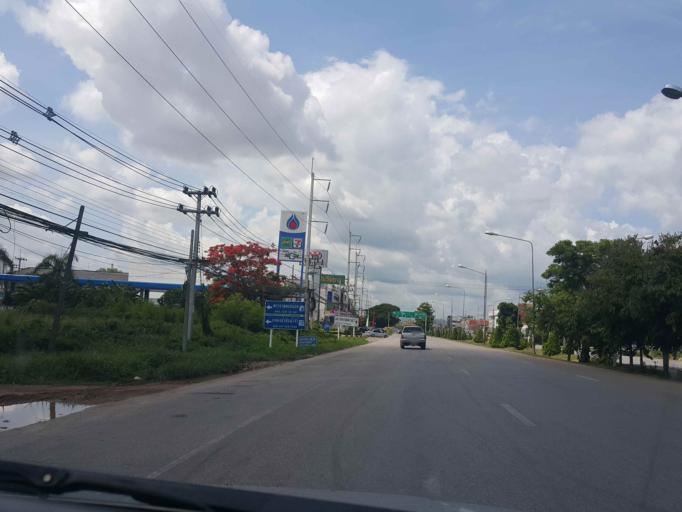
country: TH
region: Phayao
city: Phayao
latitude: 19.1465
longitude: 99.9120
